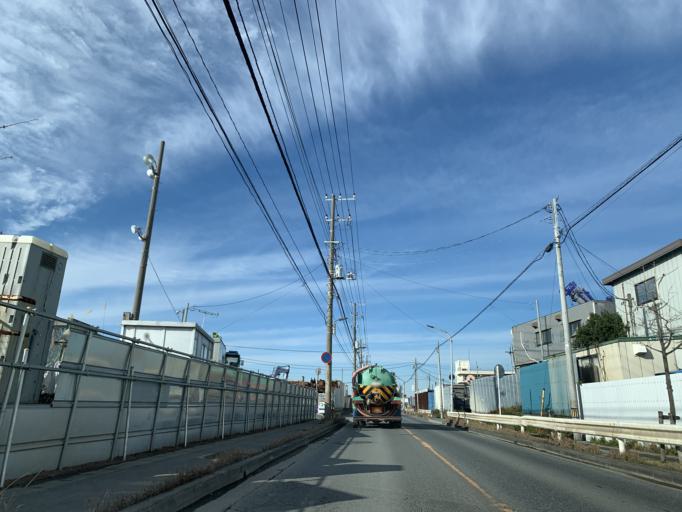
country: JP
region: Chiba
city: Funabashi
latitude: 35.6924
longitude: 139.9459
